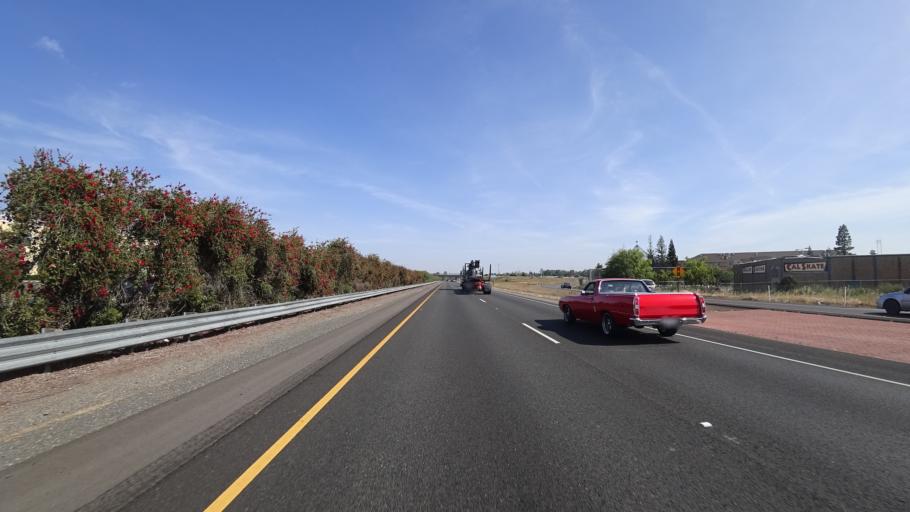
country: US
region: California
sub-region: Butte County
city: Chico
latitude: 39.7180
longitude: -121.8033
